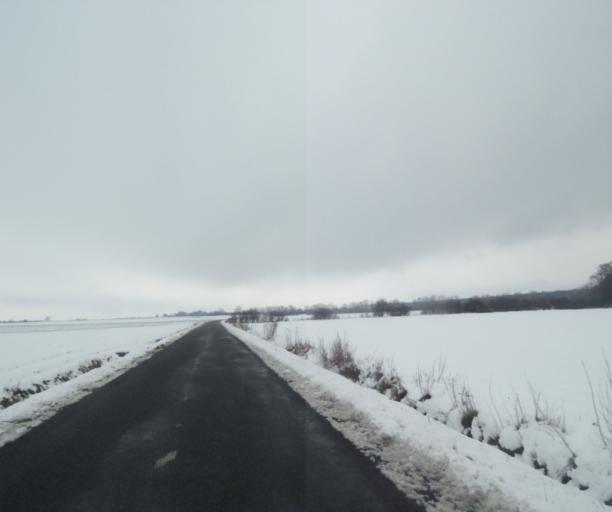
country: FR
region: Champagne-Ardenne
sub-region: Departement de la Haute-Marne
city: Montier-en-Der
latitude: 48.4700
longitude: 4.7978
